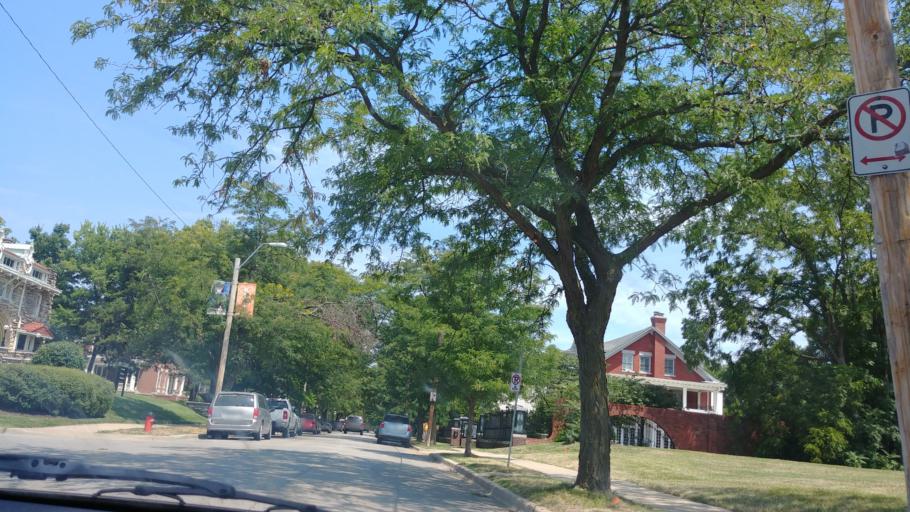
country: US
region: Kansas
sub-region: Johnson County
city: Westwood
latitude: 39.0472
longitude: -94.5820
